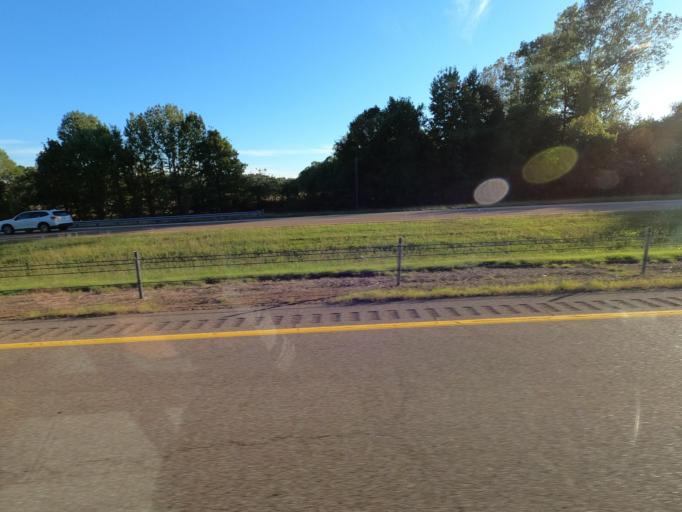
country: US
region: Tennessee
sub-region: Shelby County
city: Millington
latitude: 35.3097
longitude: -89.8460
